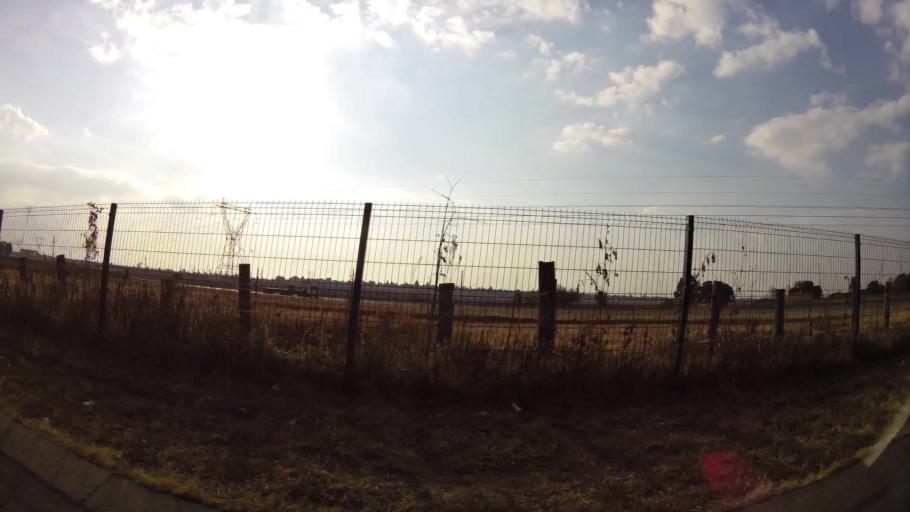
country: ZA
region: Gauteng
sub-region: City of Johannesburg Metropolitan Municipality
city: Modderfontein
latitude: -26.1097
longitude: 28.2040
